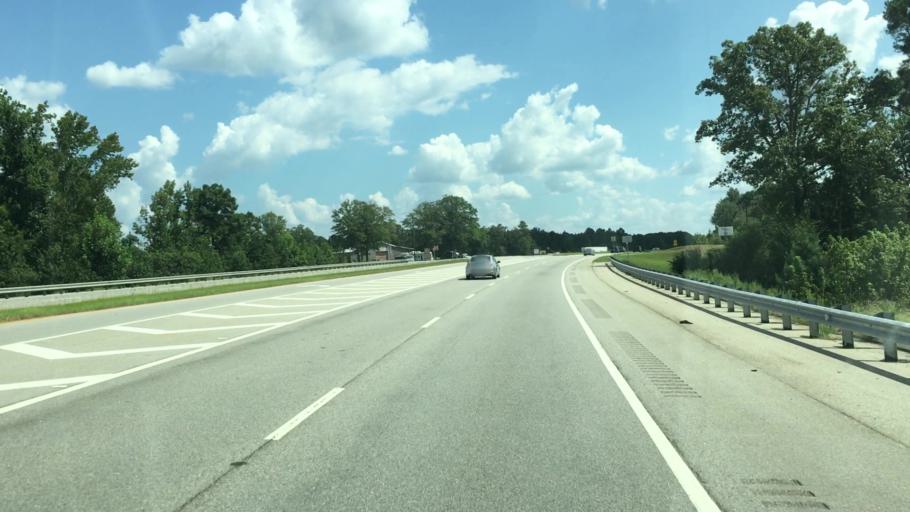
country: US
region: Georgia
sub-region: Putnam County
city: Eatonton
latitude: 33.2869
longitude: -83.3719
